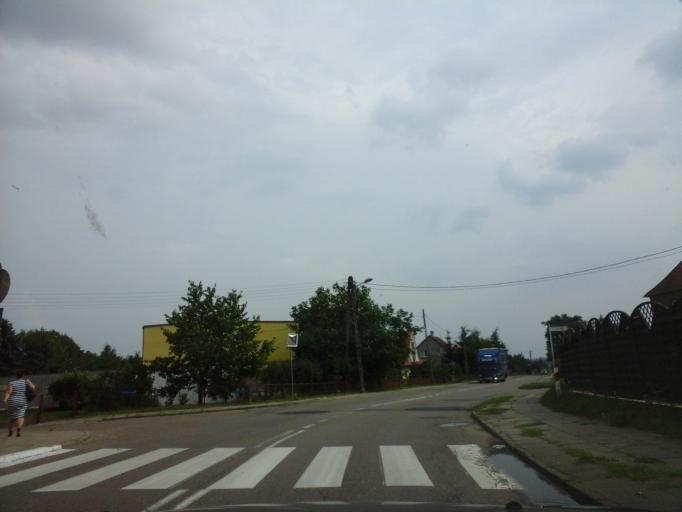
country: PL
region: Lubusz
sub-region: Powiat strzelecko-drezdenecki
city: Dobiegniew
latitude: 52.9653
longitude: 15.7508
